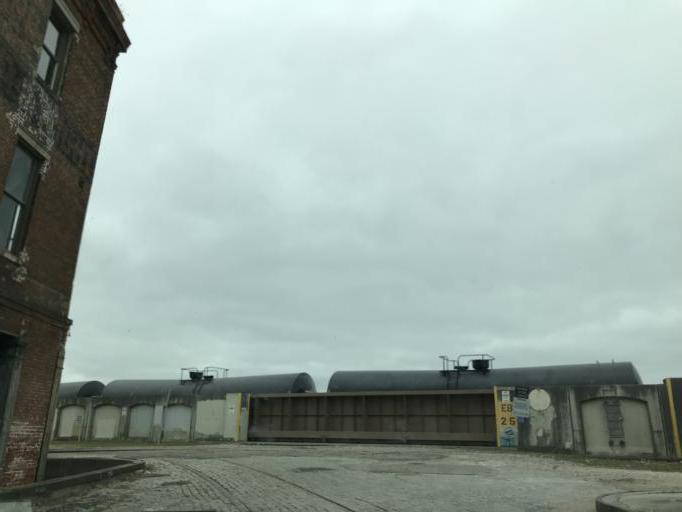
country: US
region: Louisiana
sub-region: Jefferson Parish
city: Gretna
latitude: 29.9277
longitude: -90.0659
